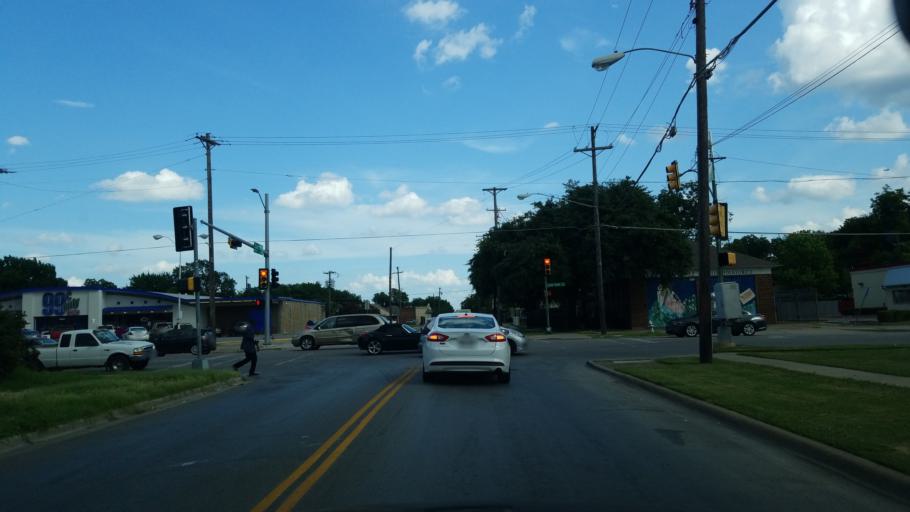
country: US
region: Texas
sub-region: Dallas County
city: Dallas
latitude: 32.7995
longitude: -96.7767
